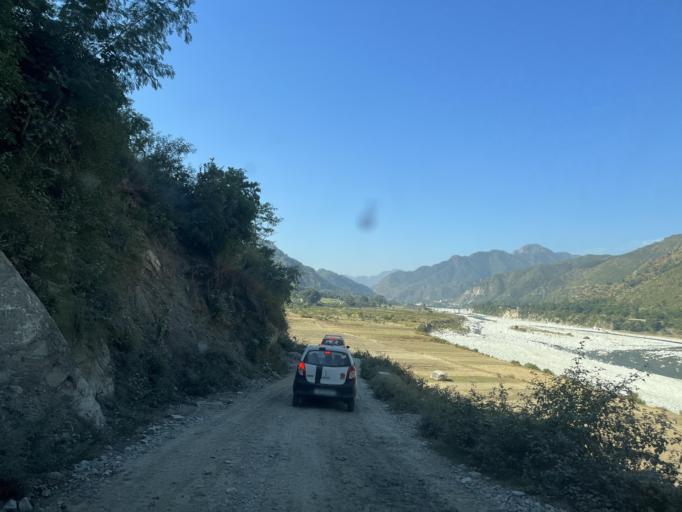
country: IN
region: Uttarakhand
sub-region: Almora
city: Ranikhet
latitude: 29.5534
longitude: 79.3943
